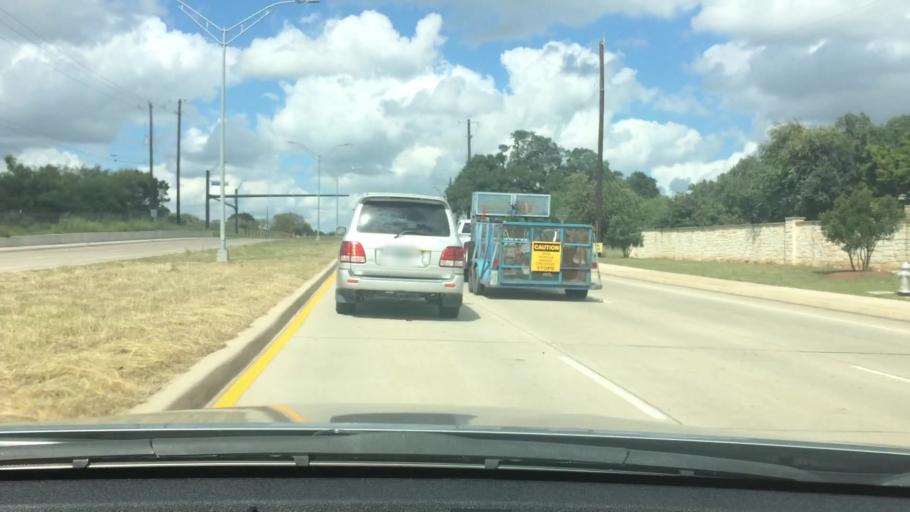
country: US
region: Texas
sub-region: Bexar County
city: Hollywood Park
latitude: 29.6150
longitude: -98.4219
